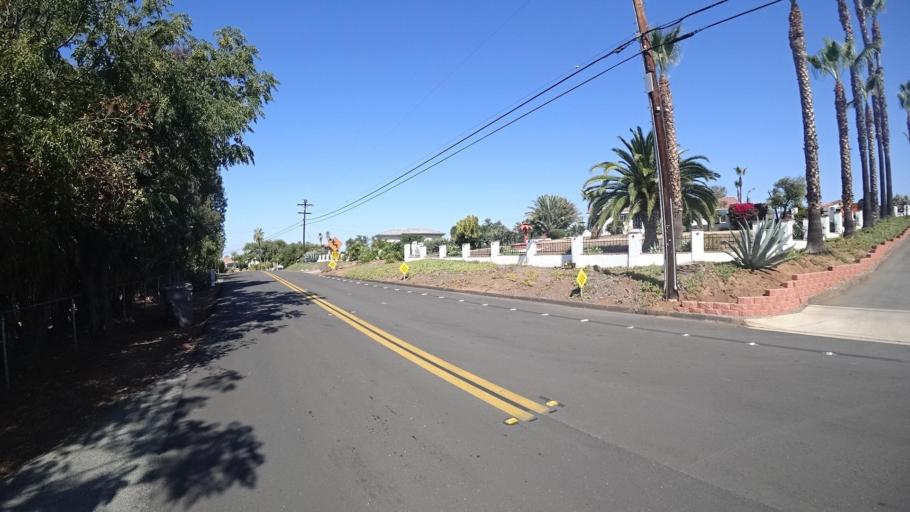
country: US
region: California
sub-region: San Diego County
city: Granite Hills
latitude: 32.7948
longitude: -116.9054
